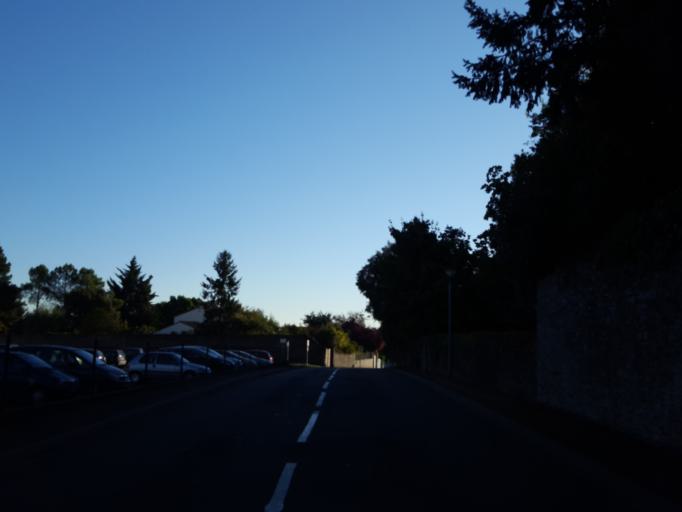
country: FR
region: Pays de la Loire
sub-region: Departement de la Loire-Atlantique
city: Basse-Goulaine
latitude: 47.2149
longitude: -1.4705
